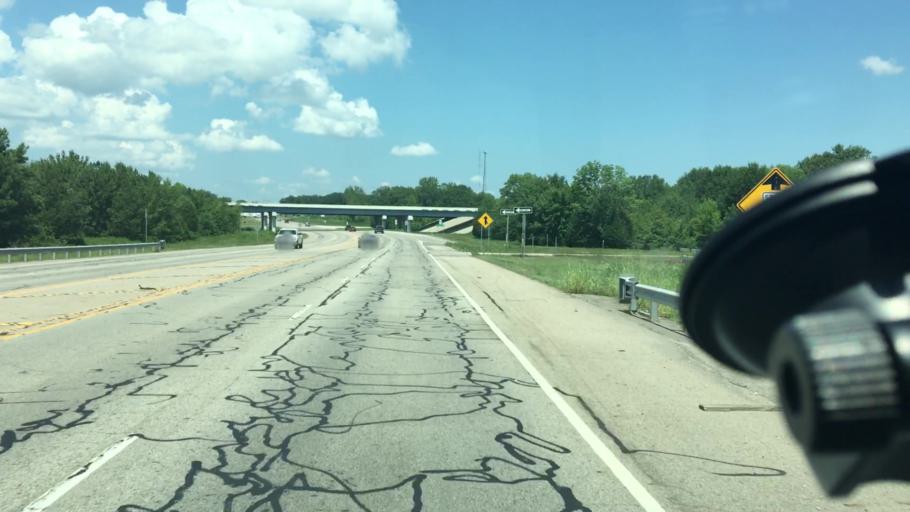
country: US
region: Arkansas
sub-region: Sebastian County
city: Barling
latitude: 35.3203
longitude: -94.2899
